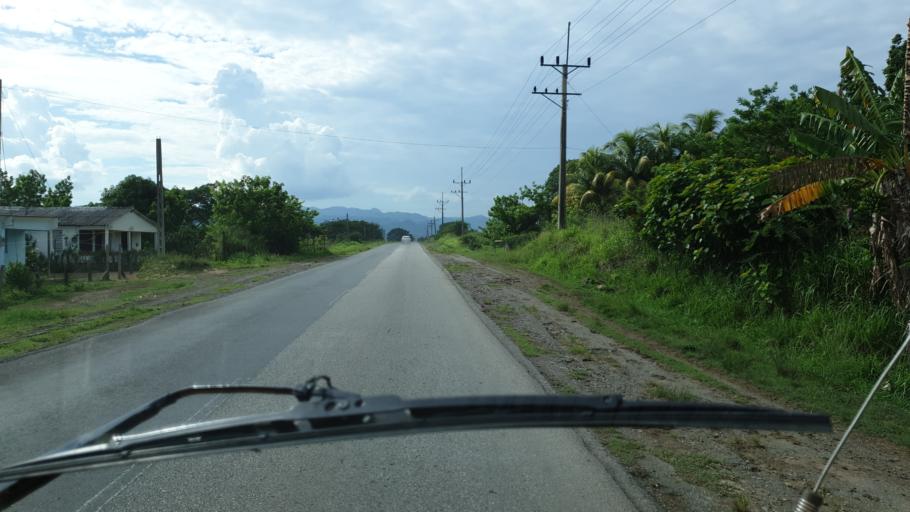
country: CU
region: Cienfuegos
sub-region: Municipio de Cienfuegos
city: Cumanayagua
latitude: 22.0733
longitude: -80.3087
